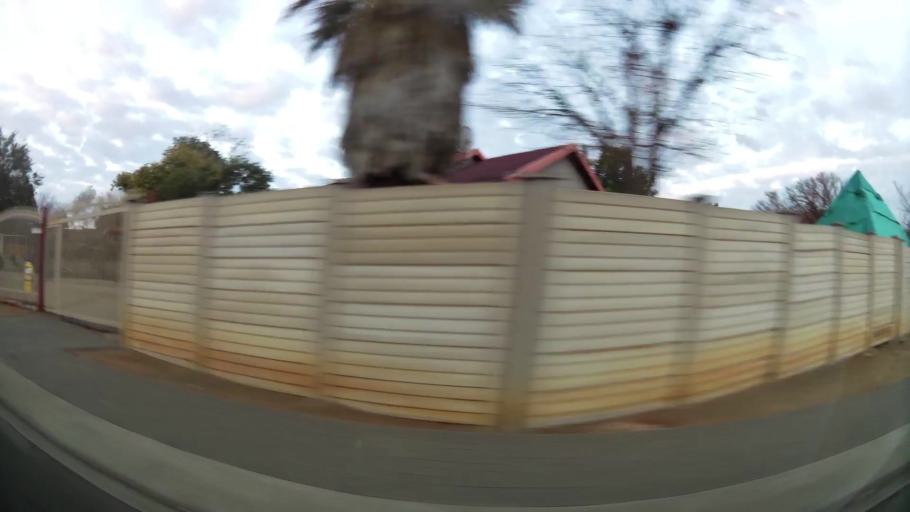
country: ZA
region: Orange Free State
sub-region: Mangaung Metropolitan Municipality
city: Bloemfontein
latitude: -29.1651
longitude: 26.1871
